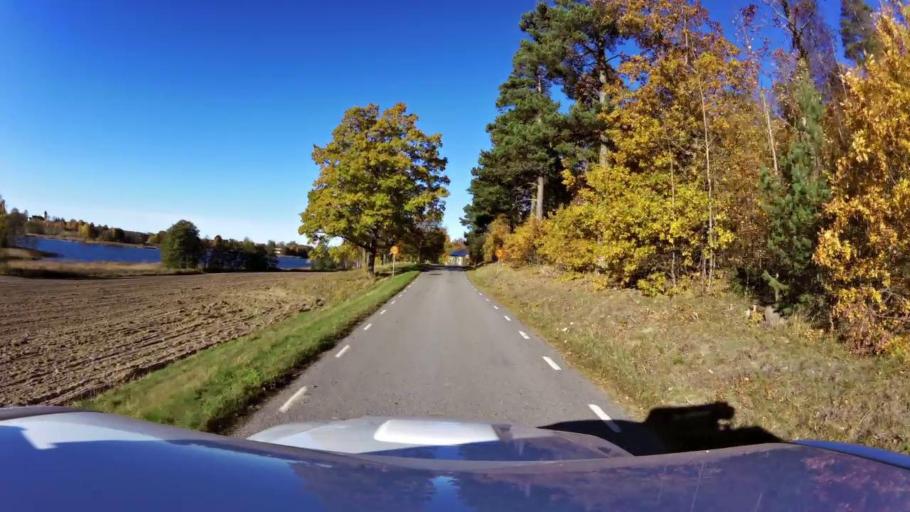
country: SE
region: OEstergoetland
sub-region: Linkopings Kommun
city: Ljungsbro
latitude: 58.5275
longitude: 15.4646
